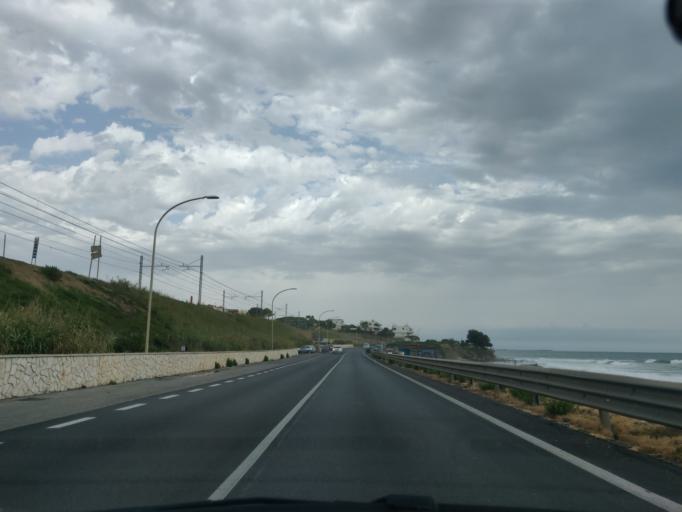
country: IT
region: Latium
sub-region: Citta metropolitana di Roma Capitale
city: Santa Marinella
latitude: 42.0403
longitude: 11.8945
